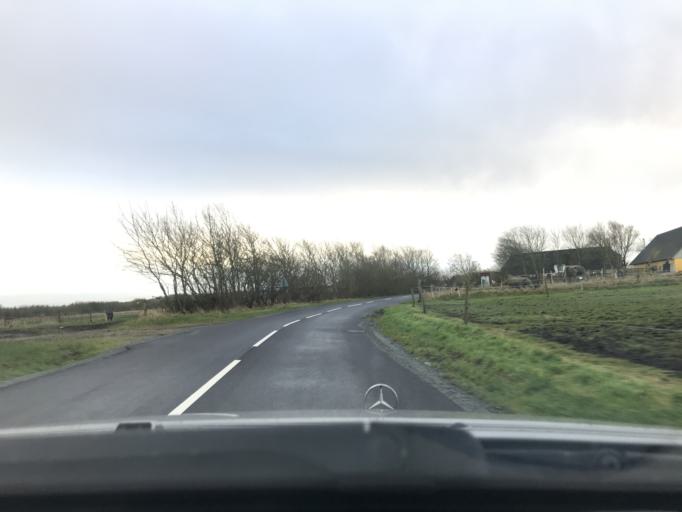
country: DK
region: South Denmark
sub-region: Esbjerg Kommune
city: Ribe
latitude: 55.3041
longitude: 8.6907
